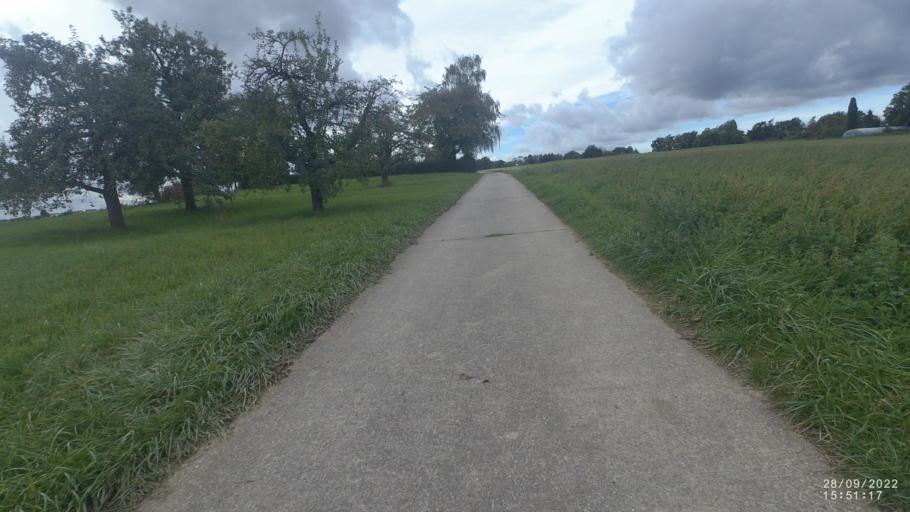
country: DE
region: Baden-Wuerttemberg
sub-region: Regierungsbezirk Stuttgart
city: Rechberghausen
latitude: 48.7347
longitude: 9.6315
